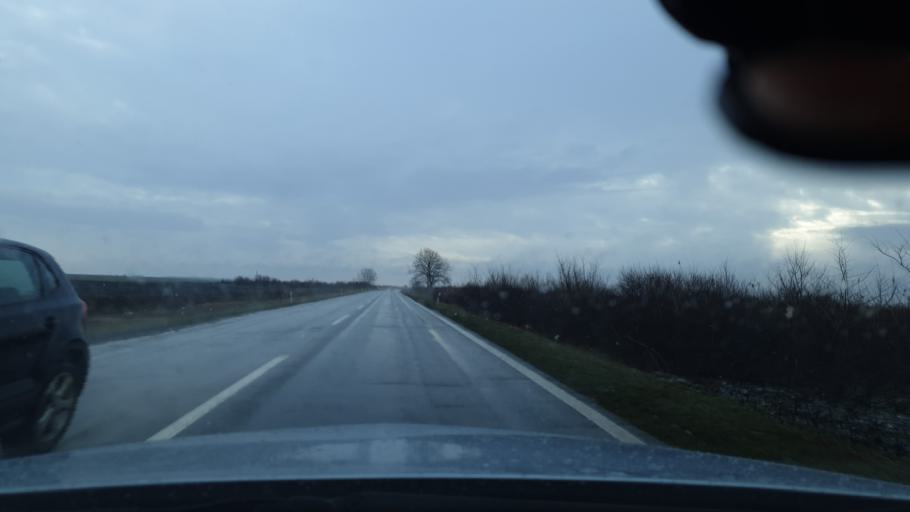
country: RS
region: Autonomna Pokrajina Vojvodina
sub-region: Juznobanatski Okrug
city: Pancevo
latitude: 44.8398
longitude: 20.8017
